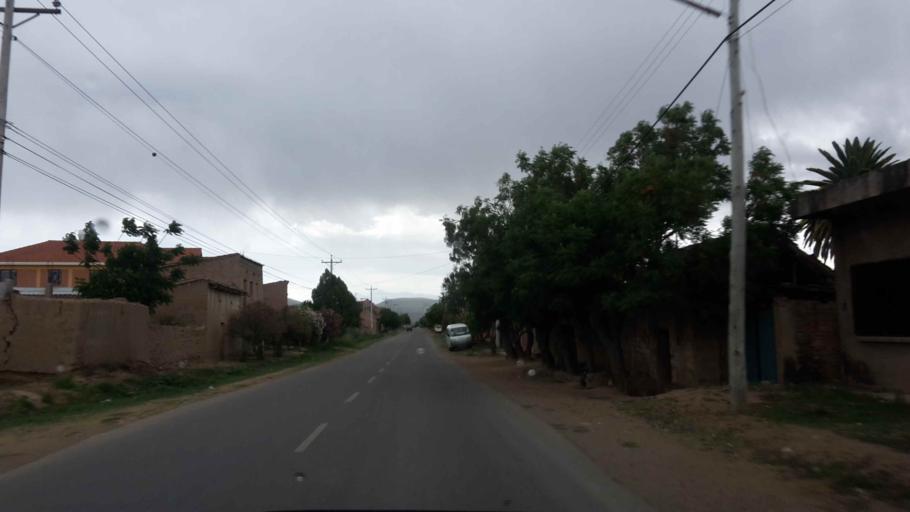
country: BO
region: Cochabamba
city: Tarata
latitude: -17.5860
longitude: -66.0507
